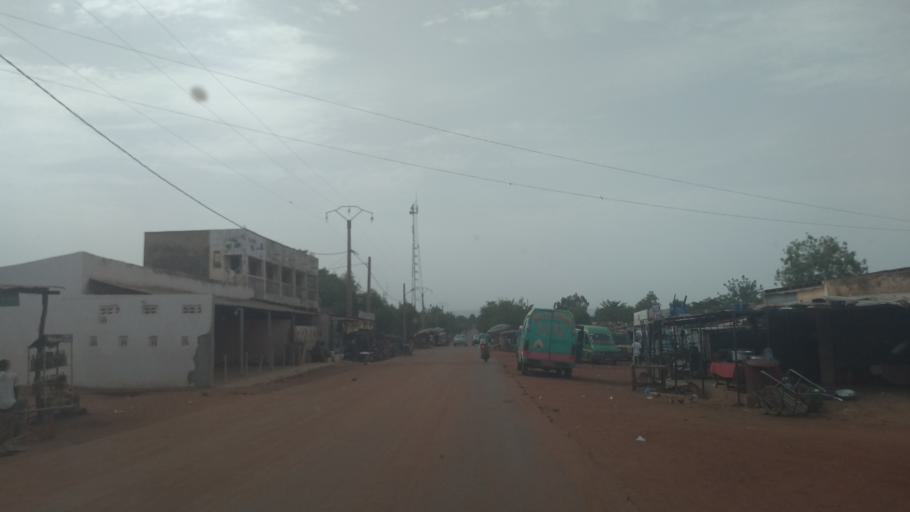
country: ML
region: Bamako
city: Bamako
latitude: 12.6150
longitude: -7.7778
